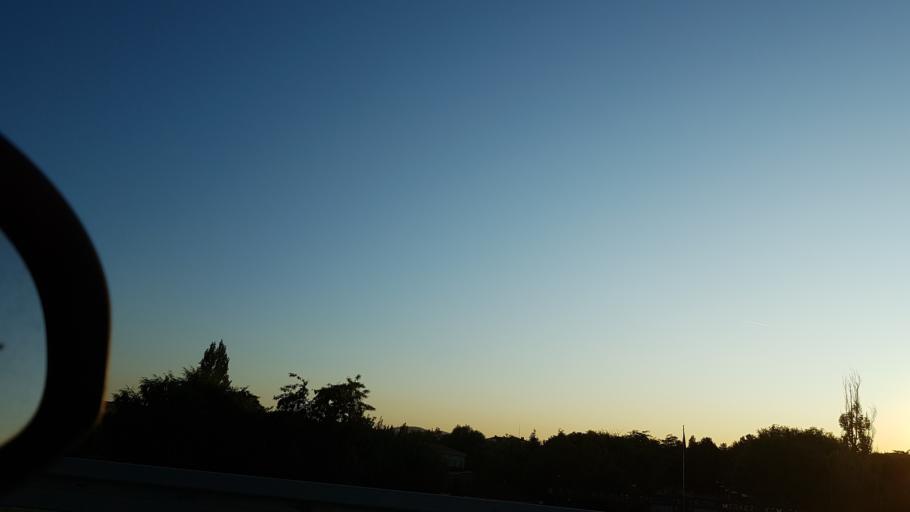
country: TR
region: Ankara
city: Batikent
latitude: 39.9272
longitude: 32.7043
